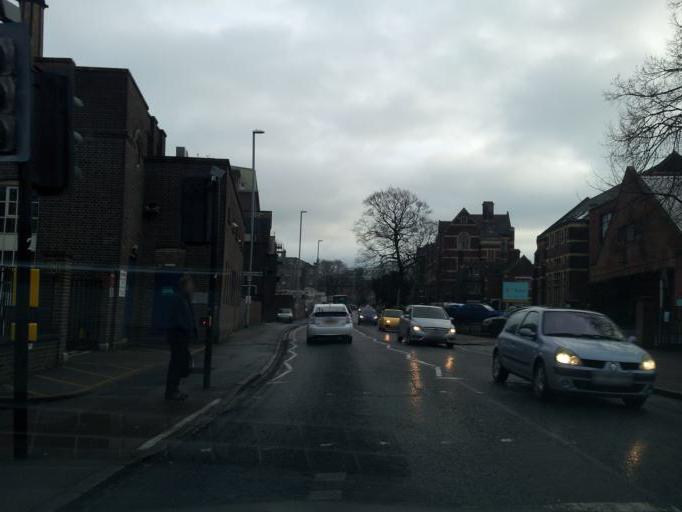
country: GB
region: England
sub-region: Cambridgeshire
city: Cambridge
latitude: 52.1974
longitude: 0.1193
